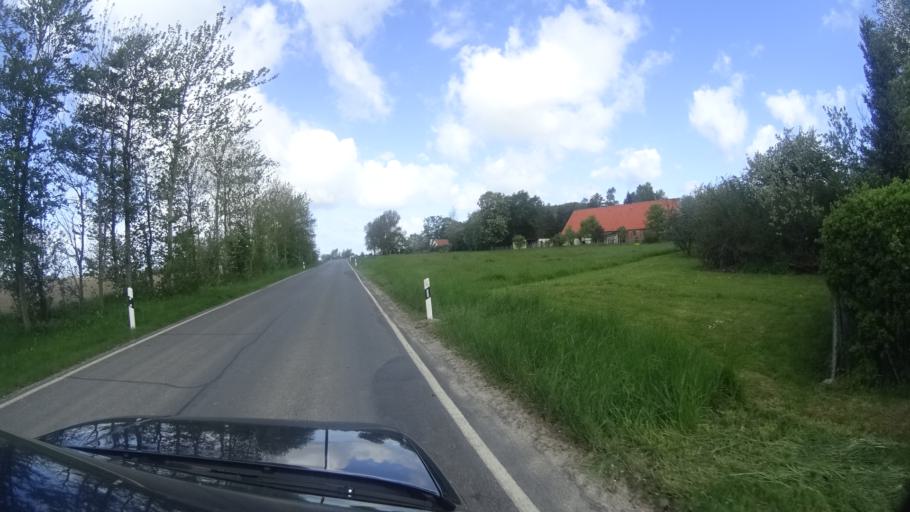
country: DE
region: Mecklenburg-Vorpommern
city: Trinwillershagen
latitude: 54.3187
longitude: 12.5806
